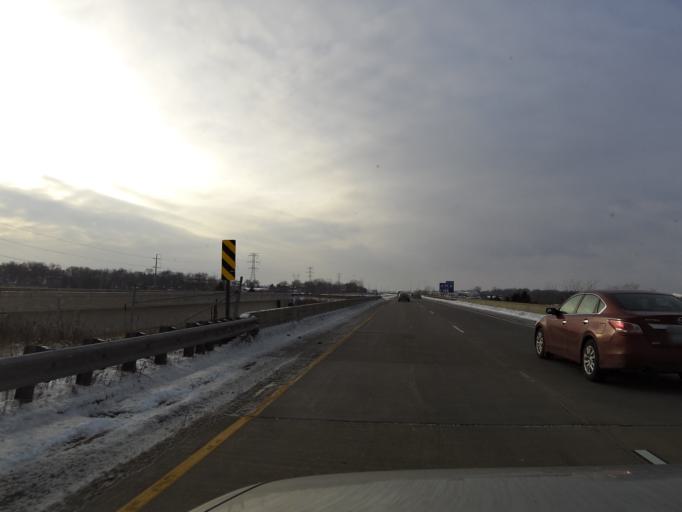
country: US
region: Minnesota
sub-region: Scott County
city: Shakopee
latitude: 44.7823
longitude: -93.4688
